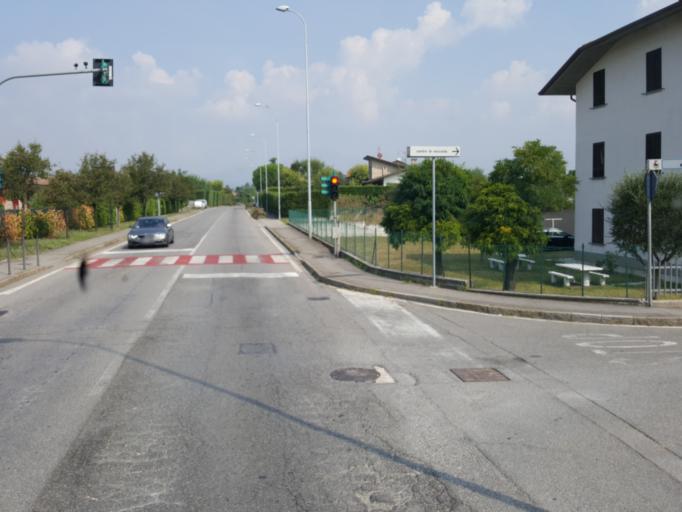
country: IT
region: Lombardy
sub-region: Provincia di Bergamo
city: Bolgare
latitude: 45.6368
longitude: 9.8081
